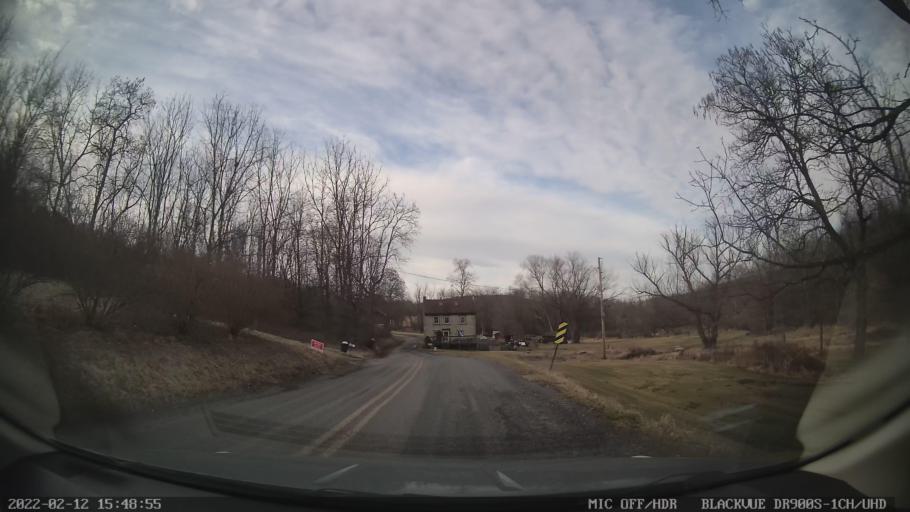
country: US
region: Pennsylvania
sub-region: Berks County
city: Kutztown
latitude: 40.5731
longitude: -75.7479
